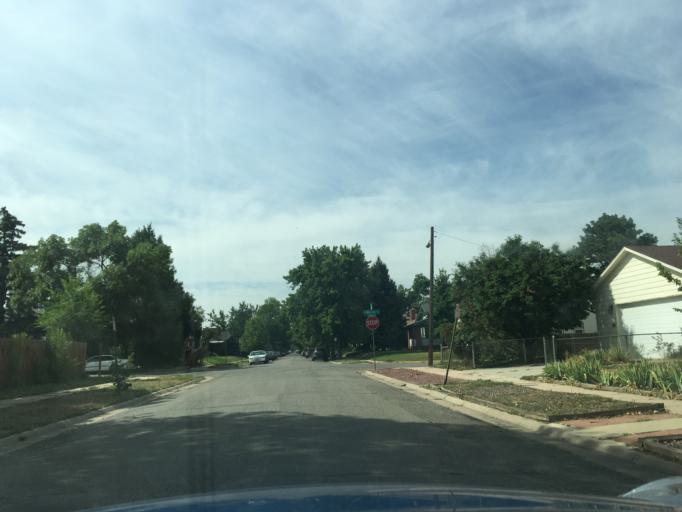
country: US
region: Colorado
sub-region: Arapahoe County
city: Englewood
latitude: 39.6771
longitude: -104.9888
